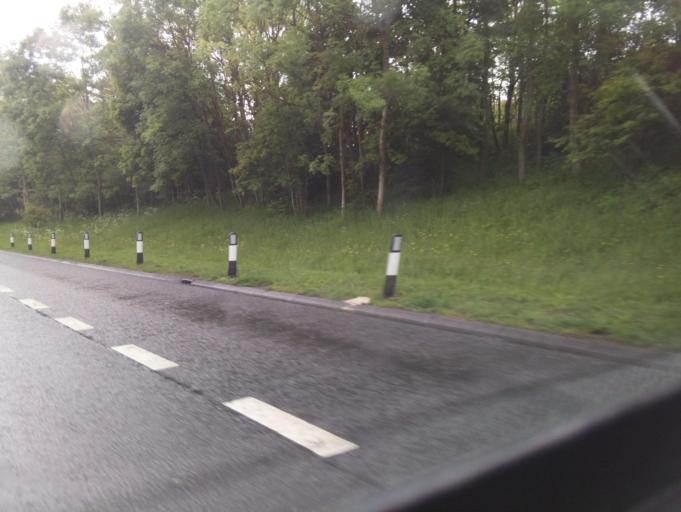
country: GB
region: England
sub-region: County Durham
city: Seaham
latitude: 54.8225
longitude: -1.3699
